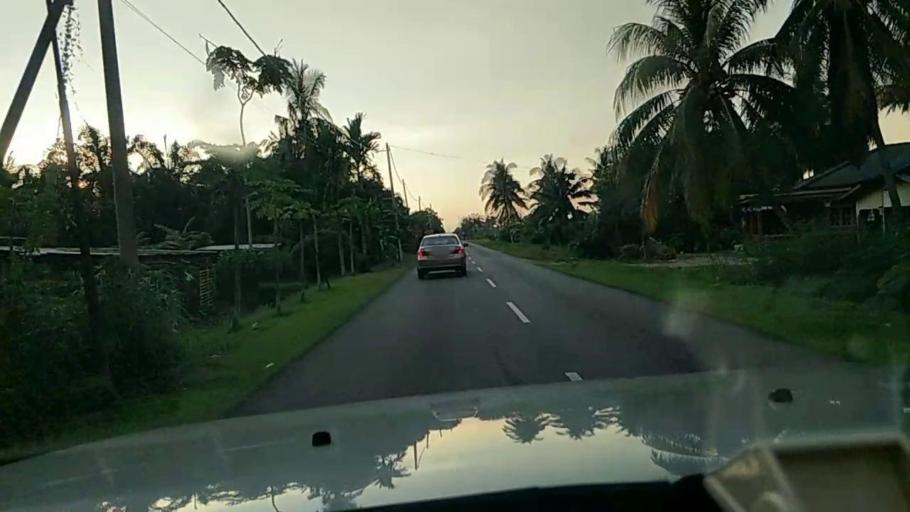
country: MY
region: Selangor
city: Kuala Selangor
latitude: 3.3149
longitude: 101.2832
